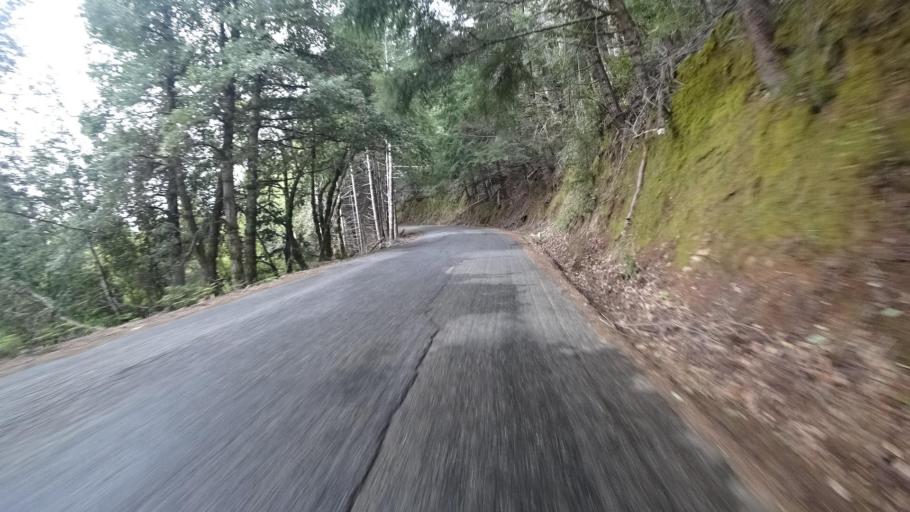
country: US
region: California
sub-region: Humboldt County
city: Redway
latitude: 40.2686
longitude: -123.7672
